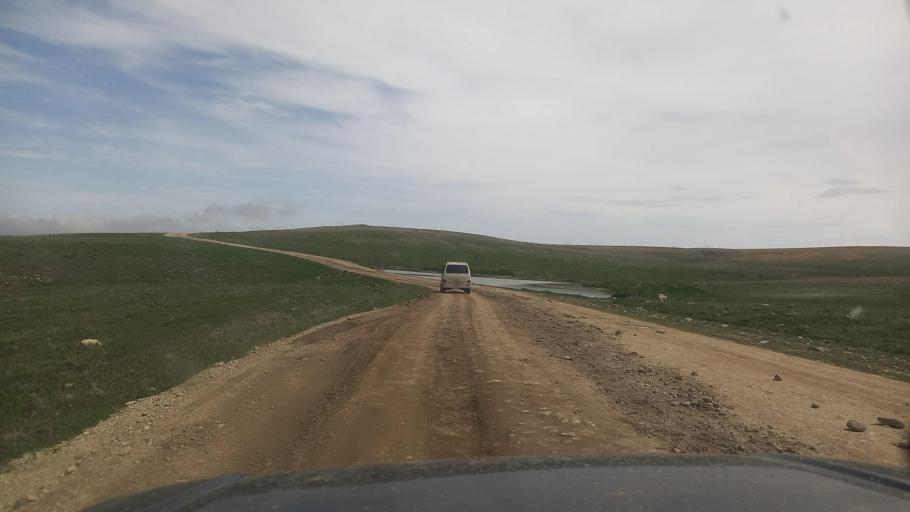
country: RU
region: Stavropol'skiy
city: Kislovodsk
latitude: 43.7622
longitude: 42.8062
